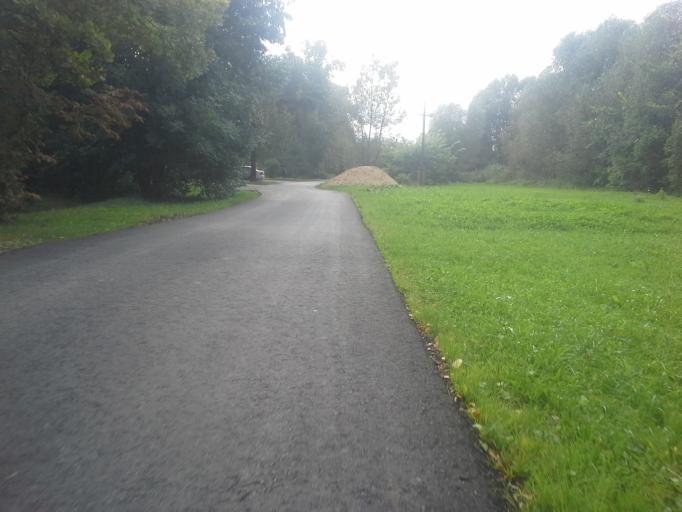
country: RU
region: Moskovskaya
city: Aprelevka
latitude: 55.5428
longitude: 37.0472
